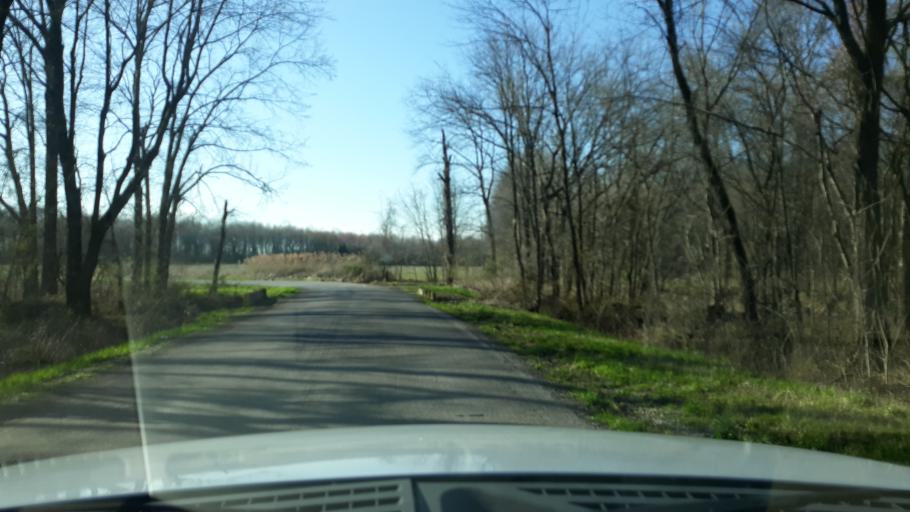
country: US
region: Illinois
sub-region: Saline County
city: Harrisburg
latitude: 37.7624
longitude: -88.5719
